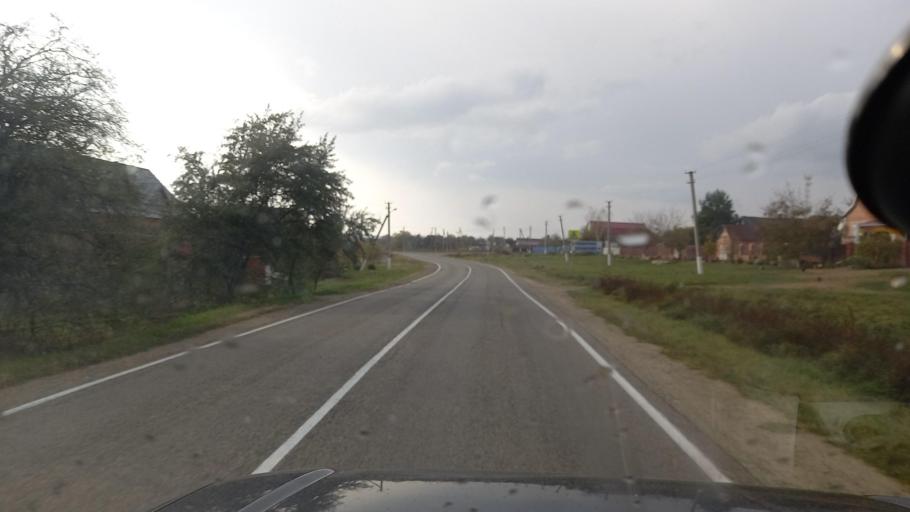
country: RU
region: Krasnodarskiy
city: Gubskaya
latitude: 44.3194
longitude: 40.6096
